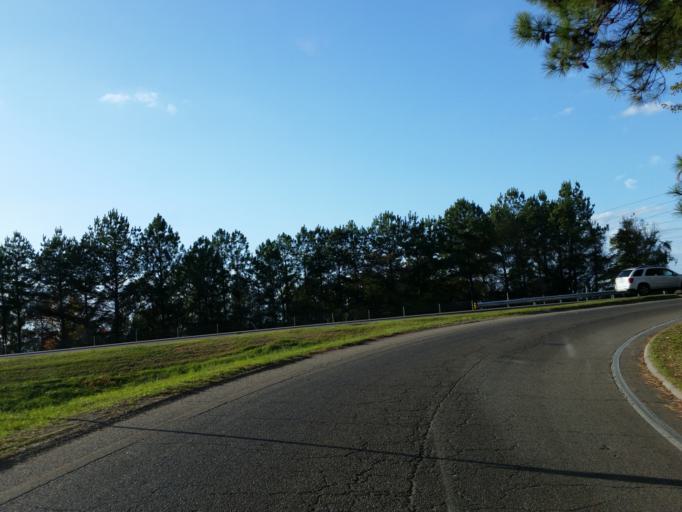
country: US
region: Mississippi
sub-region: Jones County
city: Laurel
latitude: 31.6632
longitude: -89.1589
